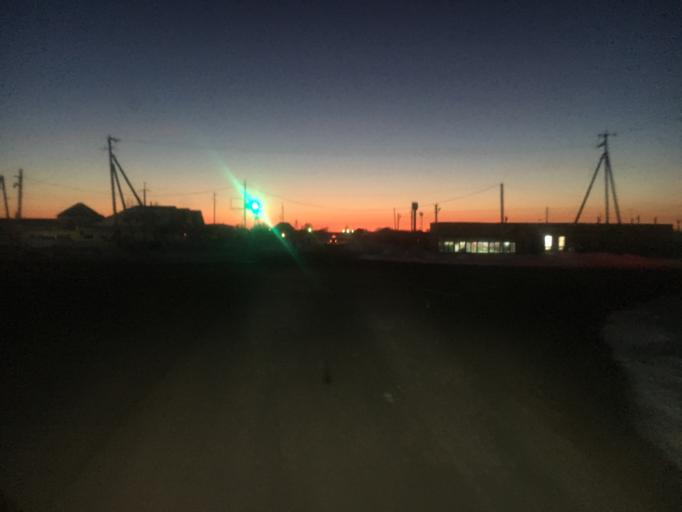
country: KZ
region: Batys Qazaqstan
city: Oral
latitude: 51.1543
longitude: 51.4897
